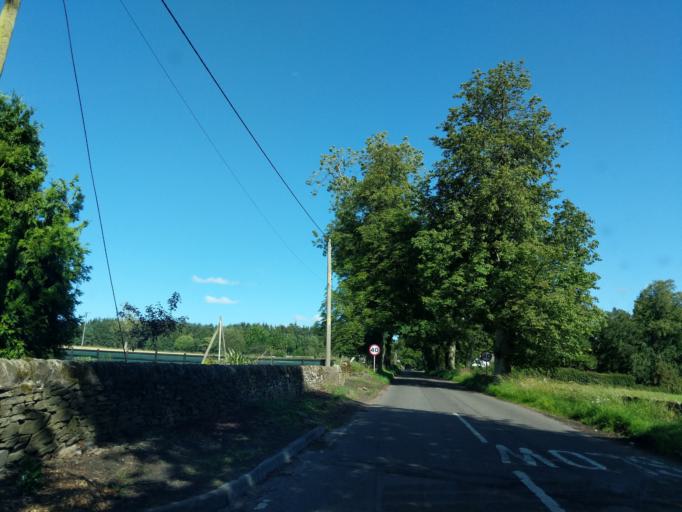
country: GB
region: Scotland
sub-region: Dundee City
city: Dundee
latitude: 56.5311
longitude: -2.9528
